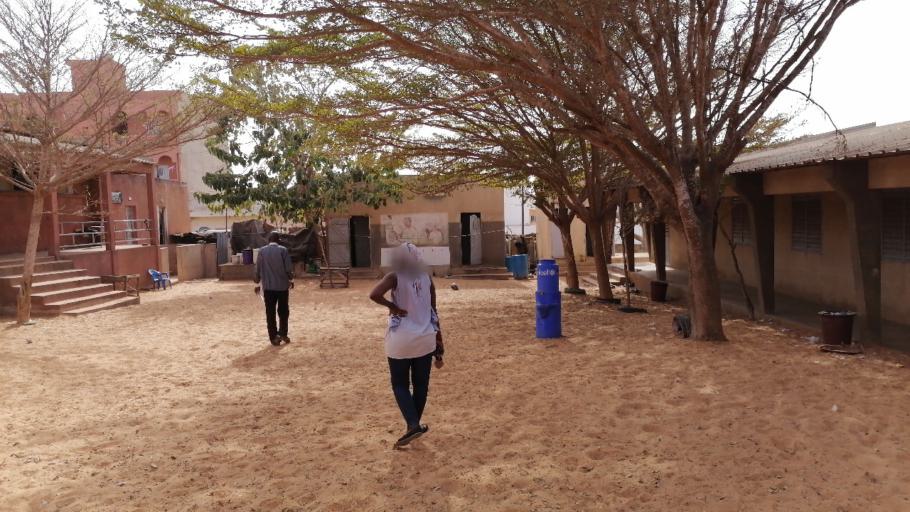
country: SN
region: Dakar
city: Pikine
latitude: 14.7811
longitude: -17.3823
